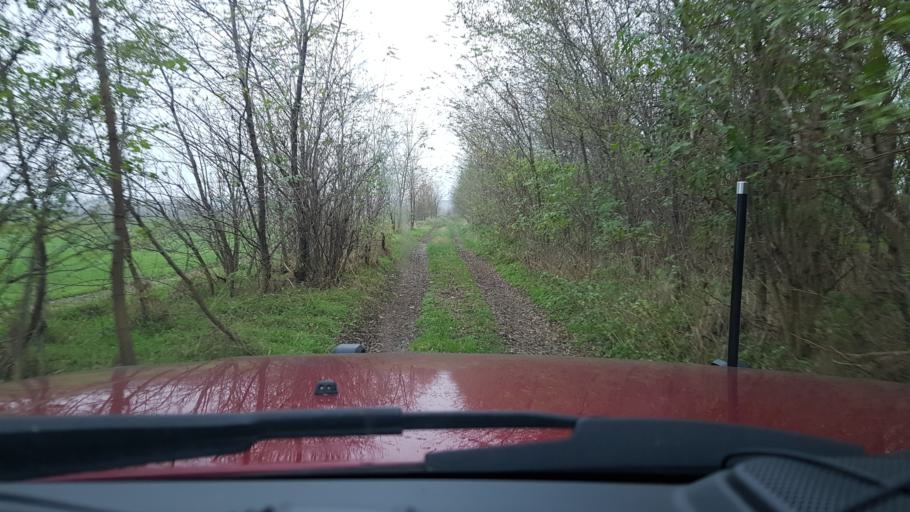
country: HU
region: Pest
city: Felsopakony
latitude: 47.3270
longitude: 19.2800
